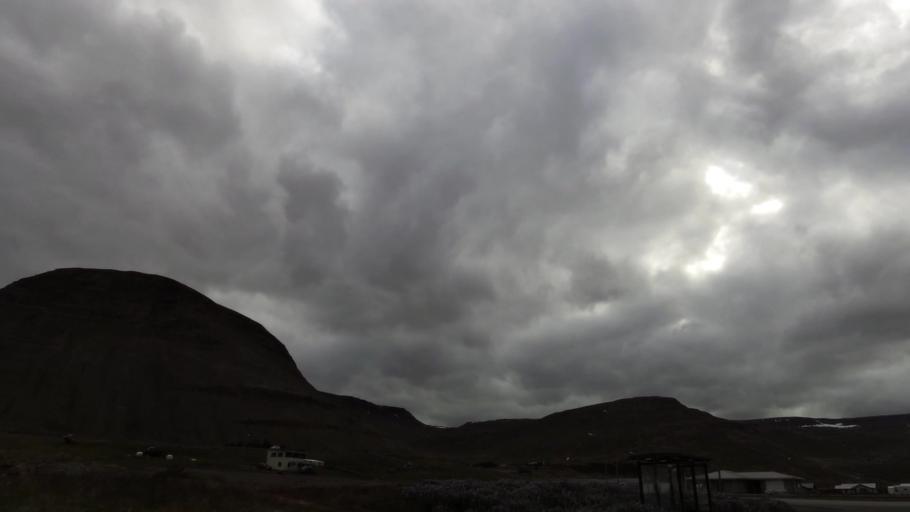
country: IS
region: Westfjords
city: Isafjoerdur
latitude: 66.0597
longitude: -23.1752
